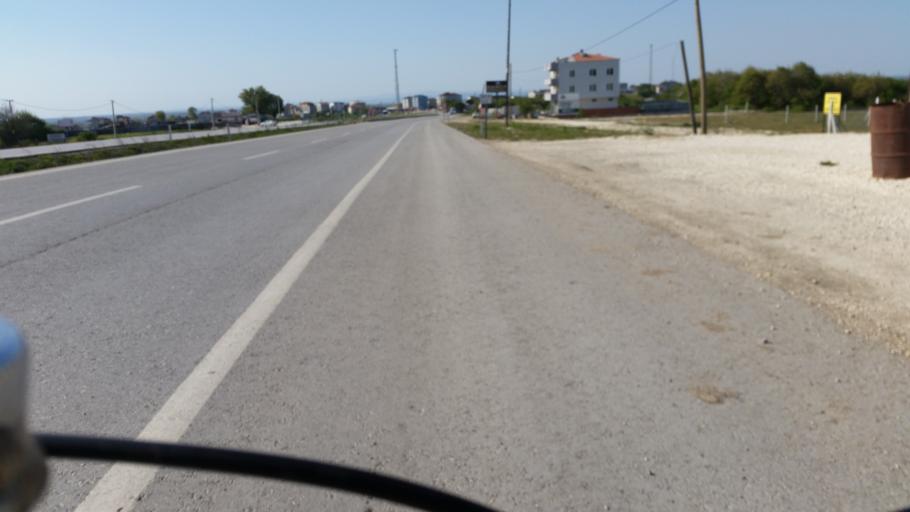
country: TR
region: Tekirdag
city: Cerkezkoey
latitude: 41.3503
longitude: 27.9580
